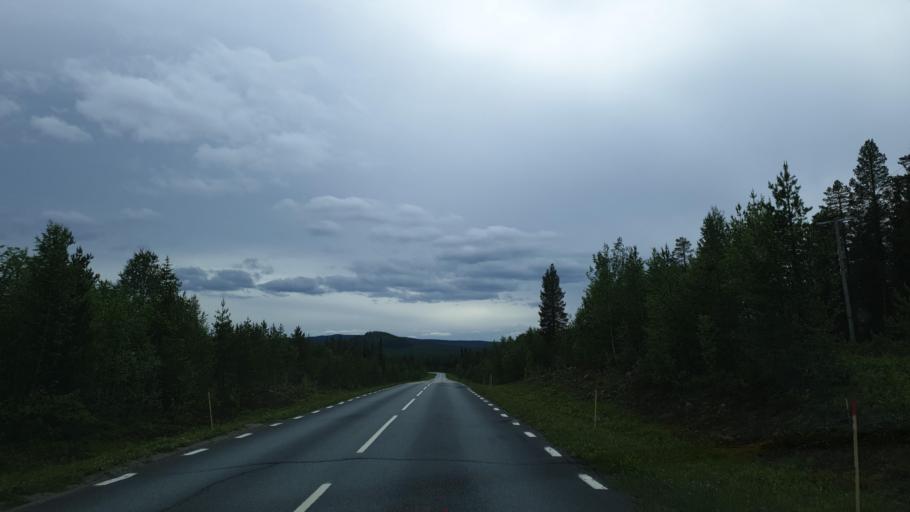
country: SE
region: Vaesterbotten
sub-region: Sorsele Kommun
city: Sorsele
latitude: 65.5330
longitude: 17.3943
